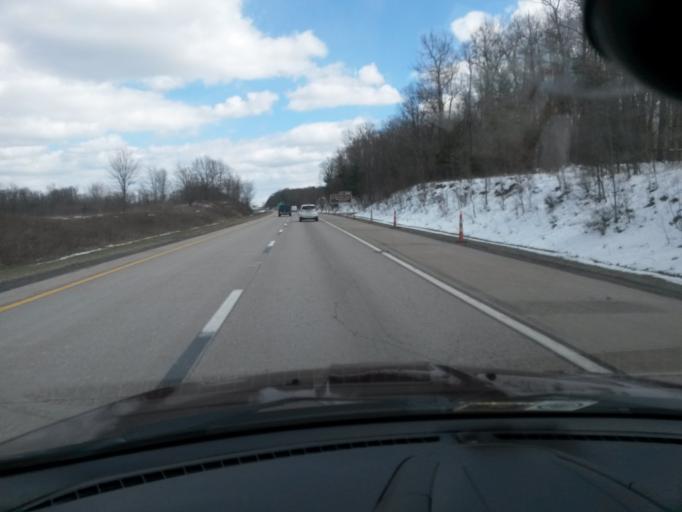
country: US
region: West Virginia
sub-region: Raleigh County
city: Daniels
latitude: 37.7738
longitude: -81.0869
